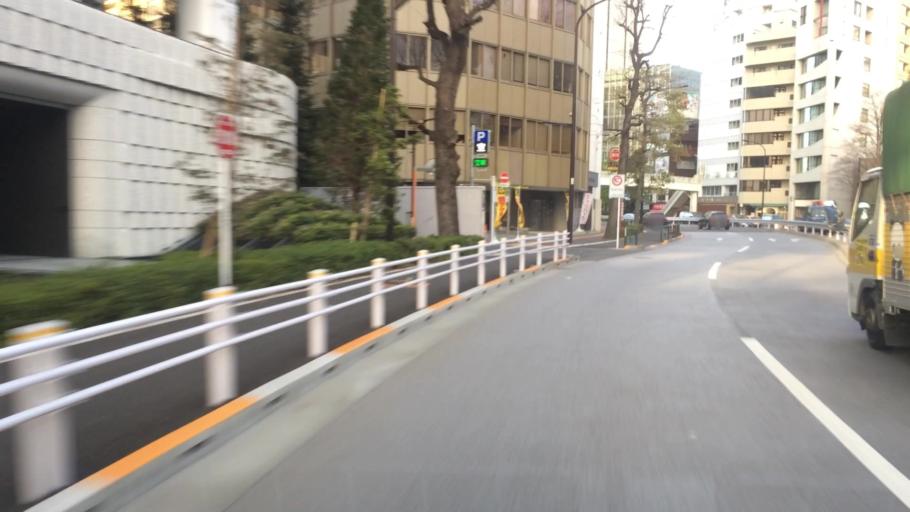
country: JP
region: Tokyo
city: Tokyo
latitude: 35.6706
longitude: 139.7238
